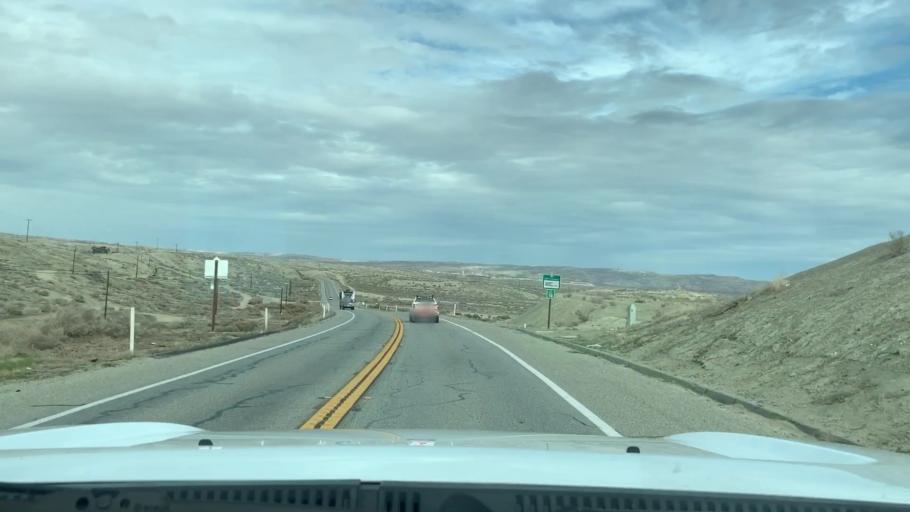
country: US
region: California
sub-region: Kern County
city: Maricopa
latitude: 35.0809
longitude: -119.4008
